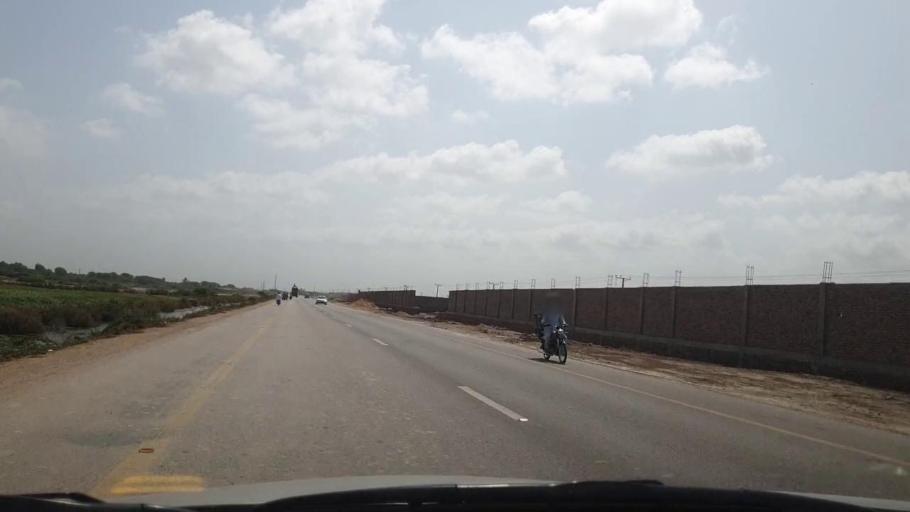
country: PK
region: Sindh
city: Talhar
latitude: 24.9005
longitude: 68.7662
